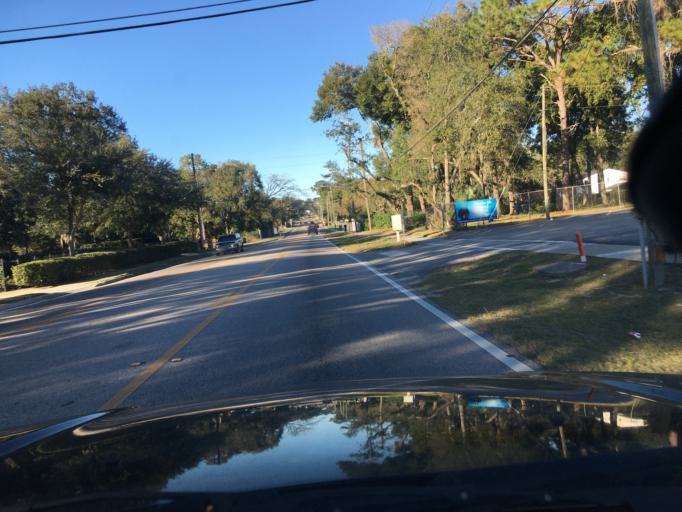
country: US
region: Florida
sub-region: Orange County
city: Pine Hills
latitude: 28.5866
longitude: -81.4678
